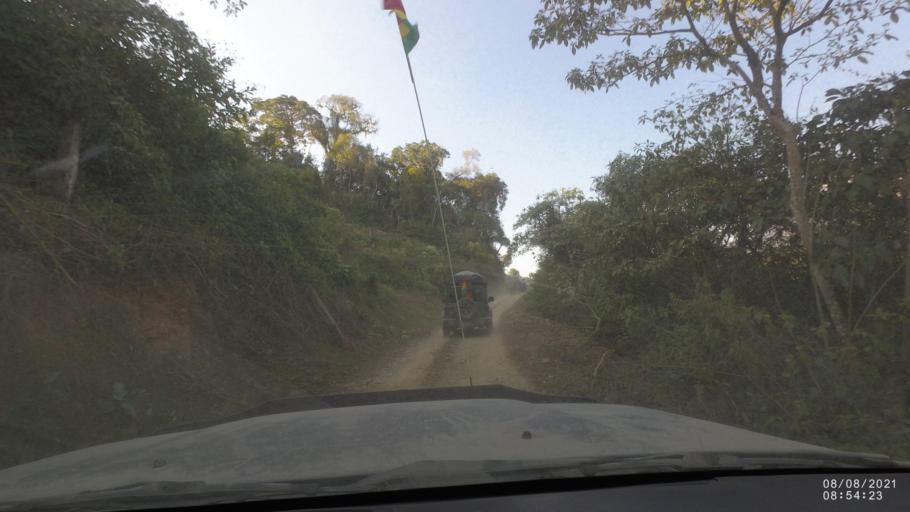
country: BO
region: La Paz
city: Quime
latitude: -16.5427
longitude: -66.7516
